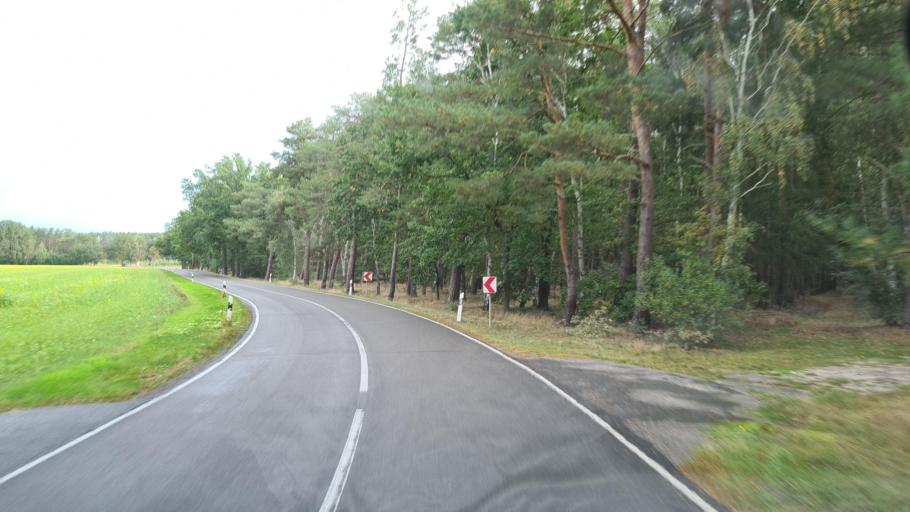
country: DE
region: Brandenburg
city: Kasel-Golzig
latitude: 51.9145
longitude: 13.7138
